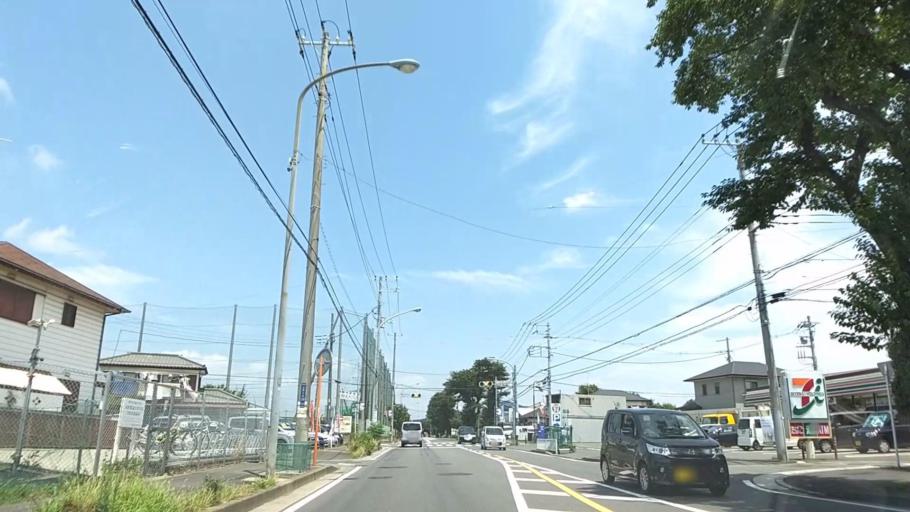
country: JP
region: Kanagawa
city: Minami-rinkan
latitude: 35.4804
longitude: 139.4805
